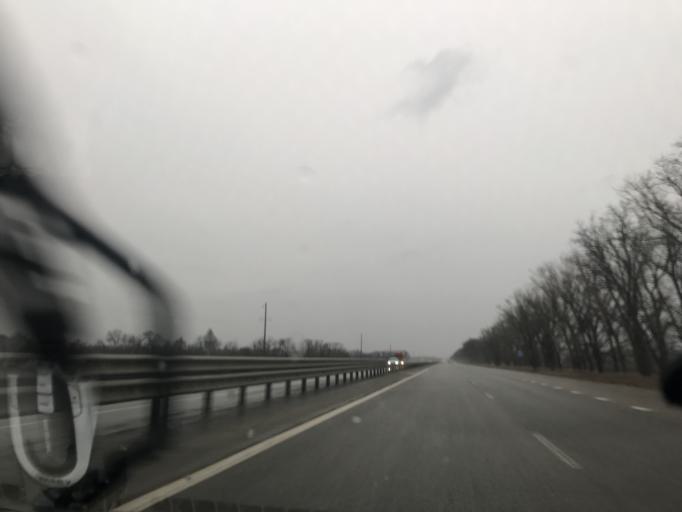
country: RU
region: Krasnodarskiy
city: Kislyakovskaya
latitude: 46.3733
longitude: 39.7524
